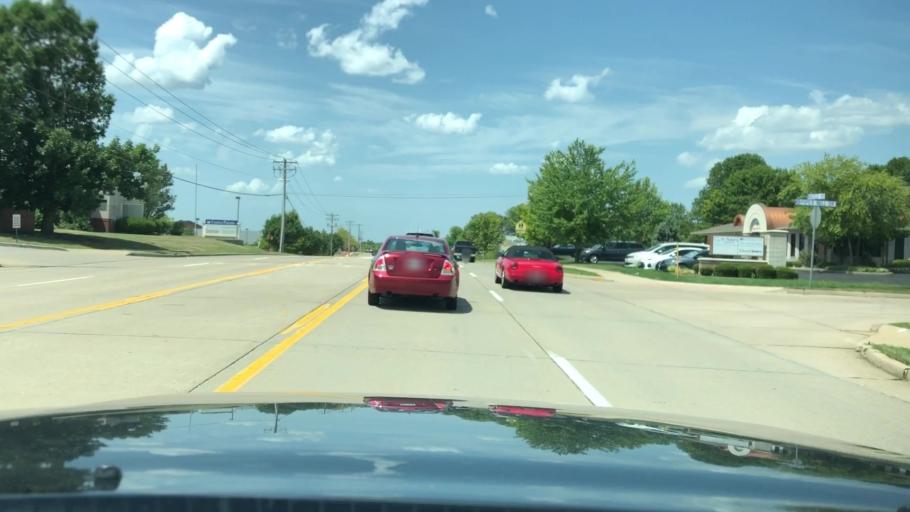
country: US
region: Missouri
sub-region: Saint Charles County
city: Saint Peters
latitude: 38.7925
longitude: -90.5882
